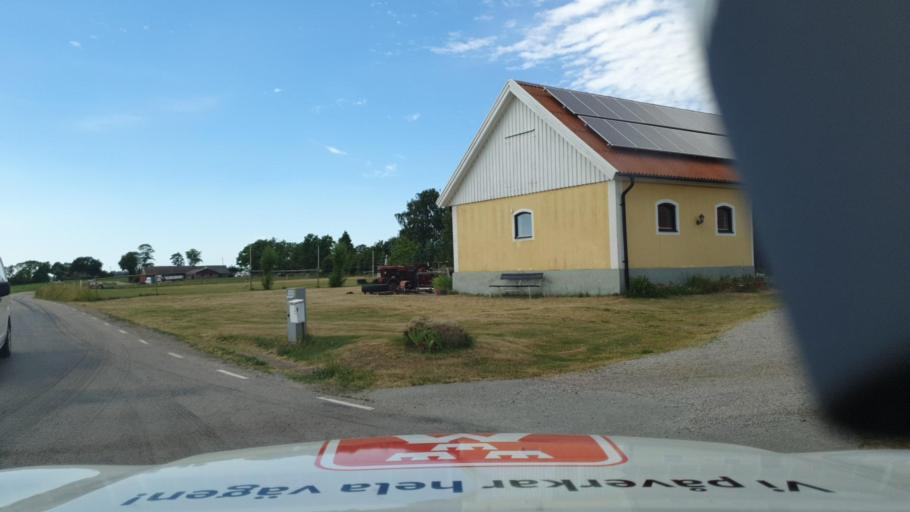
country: SE
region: Skane
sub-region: Sjobo Kommun
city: Sjoebo
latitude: 55.6355
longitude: 13.8085
